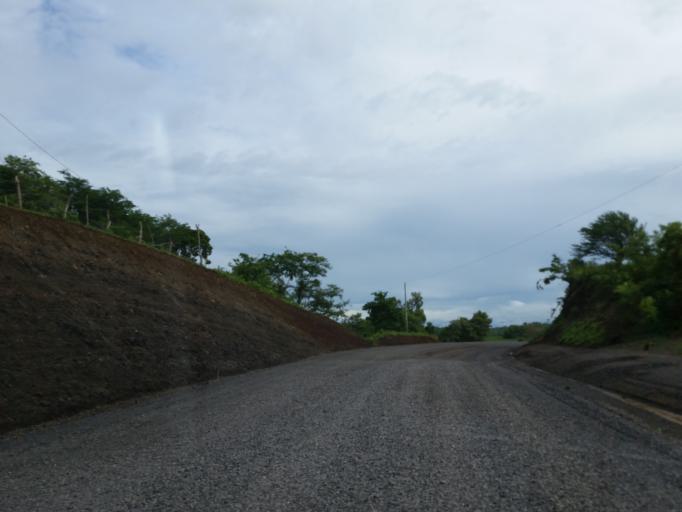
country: NI
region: Leon
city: La Paz Centro
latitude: 12.4006
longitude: -86.6560
